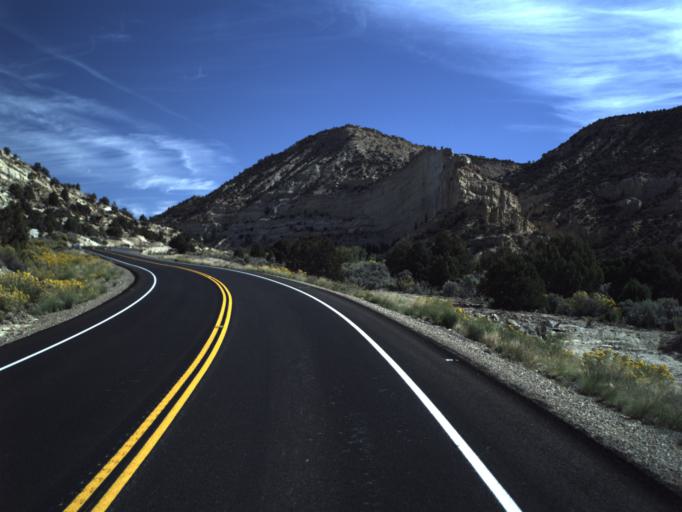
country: US
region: Utah
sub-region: Garfield County
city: Panguitch
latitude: 37.5922
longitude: -111.9287
